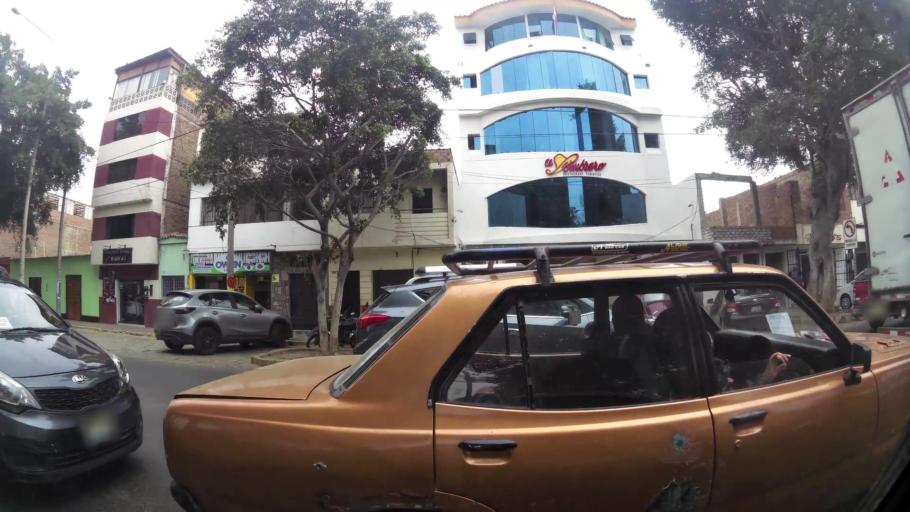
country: PE
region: La Libertad
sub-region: Provincia de Trujillo
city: Trujillo
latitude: -8.1075
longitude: -79.0318
